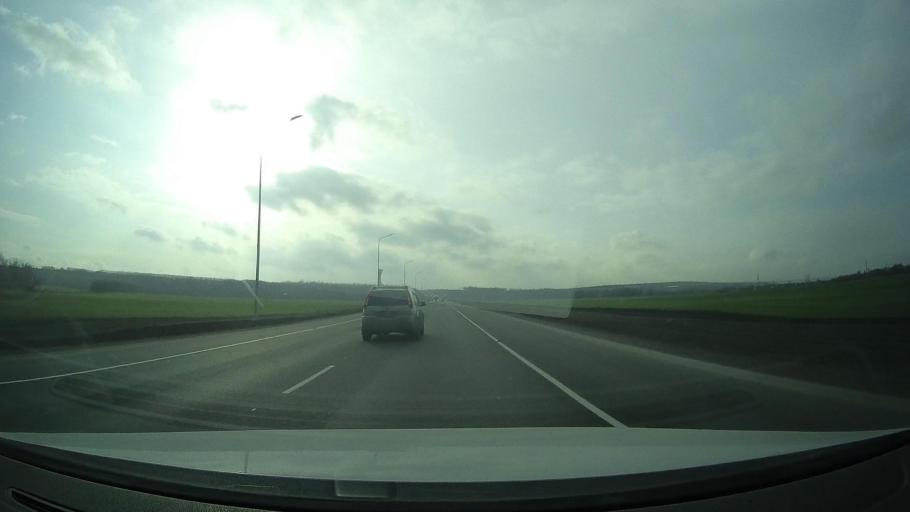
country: RU
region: Rostov
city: Grushevskaya
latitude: 47.4440
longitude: 39.8762
